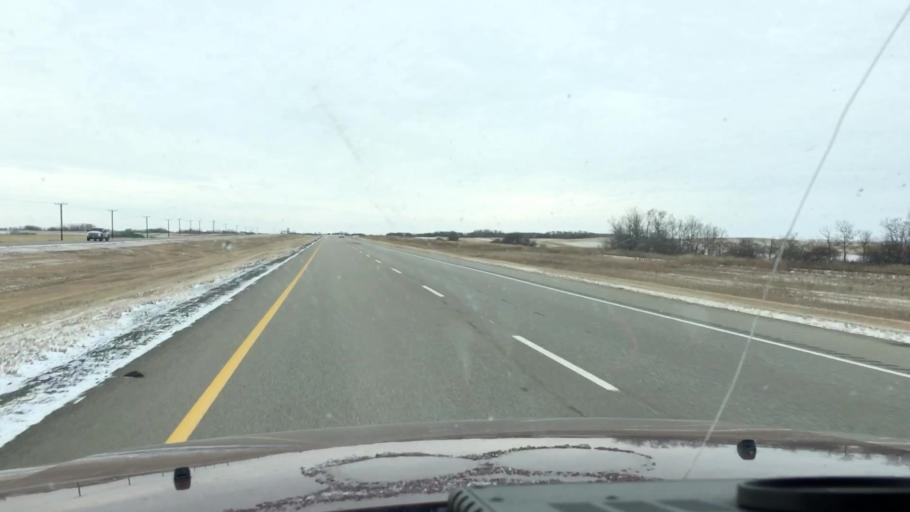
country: CA
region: Saskatchewan
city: Watrous
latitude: 51.3967
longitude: -106.1725
